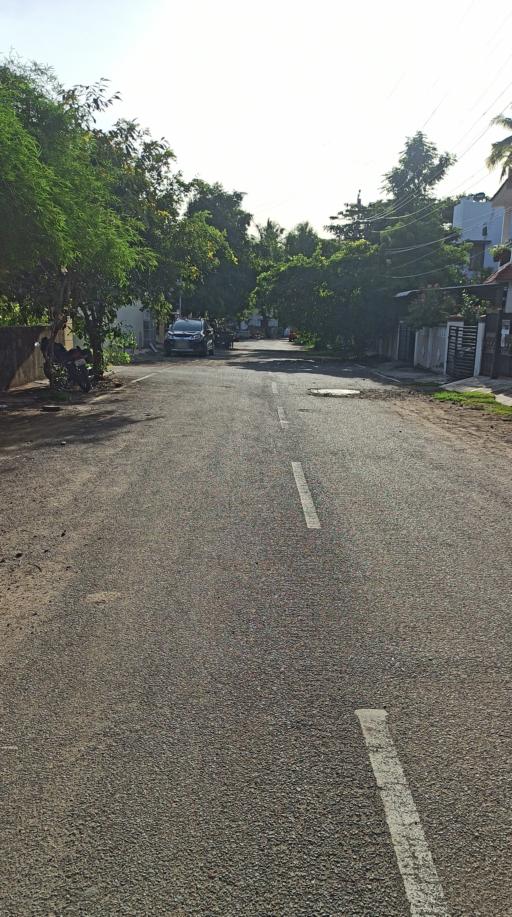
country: IN
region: Tamil Nadu
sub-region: Kancheepuram
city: Vandalur
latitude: 12.9308
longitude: 80.1069
